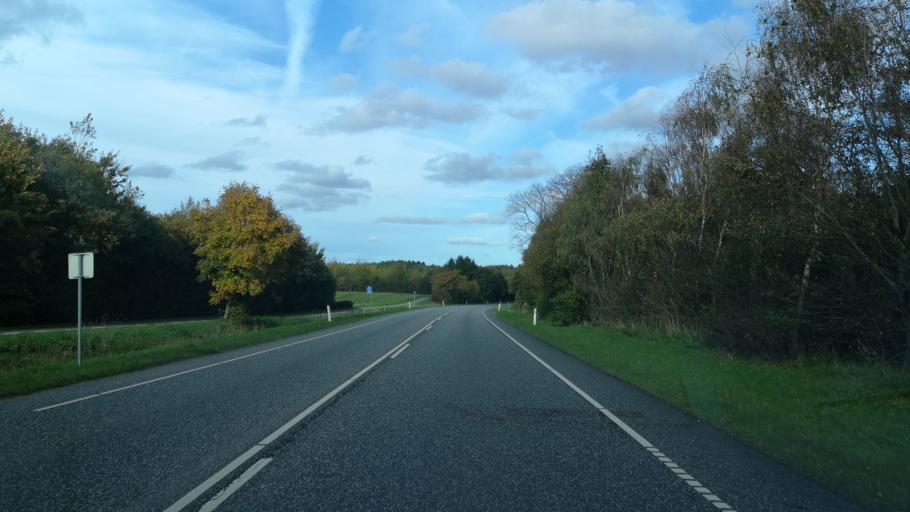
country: DK
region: Central Jutland
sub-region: Holstebro Kommune
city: Holstebro
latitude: 56.3342
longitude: 8.6108
